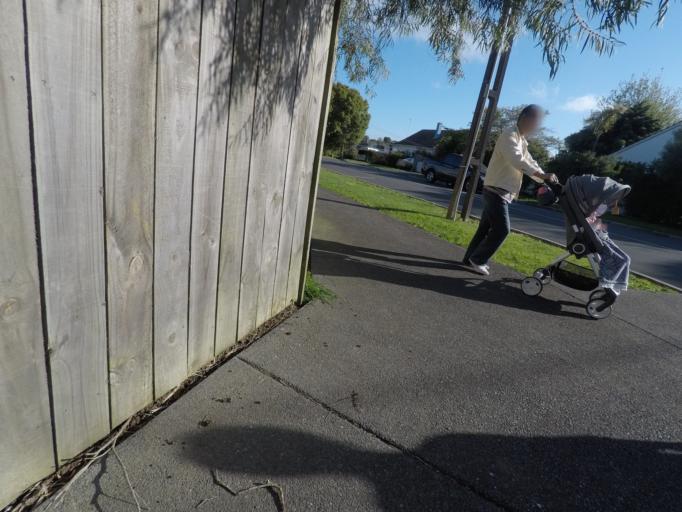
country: NZ
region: Auckland
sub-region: Auckland
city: Rosebank
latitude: -36.8990
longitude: 174.7159
